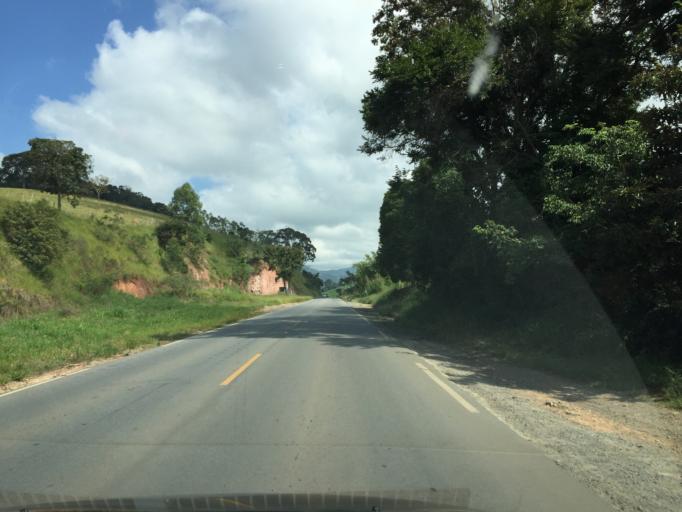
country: BR
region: Minas Gerais
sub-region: Passa Quatro
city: Passa Quatro
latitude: -22.3671
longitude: -44.9575
